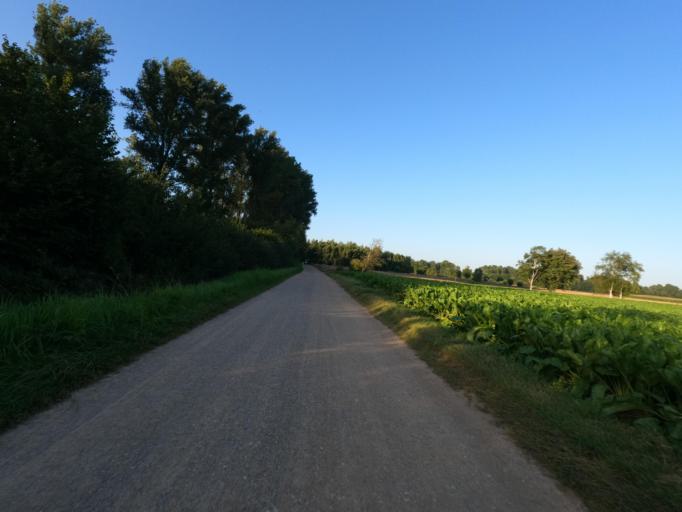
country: DE
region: North Rhine-Westphalia
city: Julich
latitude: 50.9416
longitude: 6.3235
